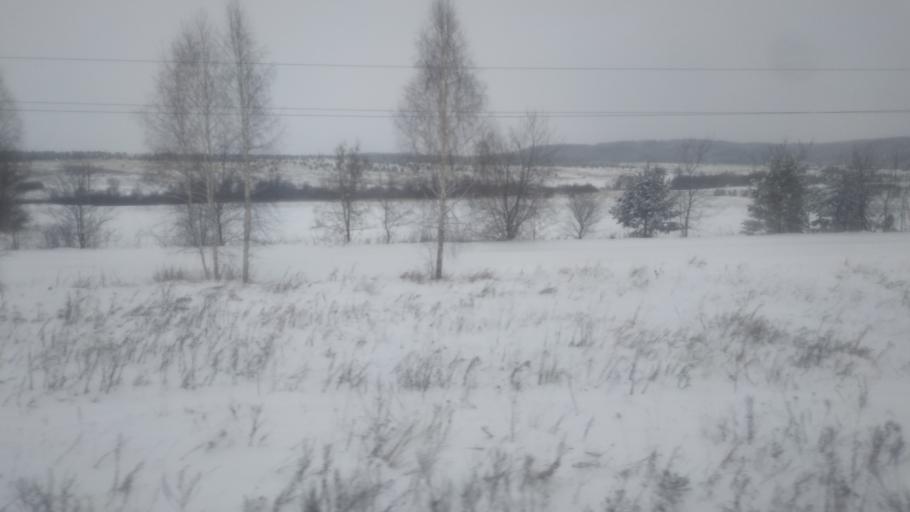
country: RU
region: Udmurtiya
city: Kiyasovo
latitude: 56.4981
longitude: 53.4075
